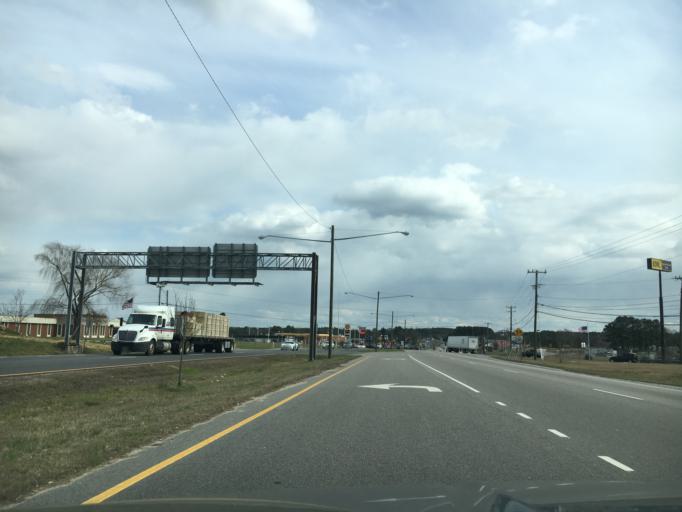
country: US
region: Virginia
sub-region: Mecklenburg County
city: South Hill
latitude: 36.7123
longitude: -78.1117
